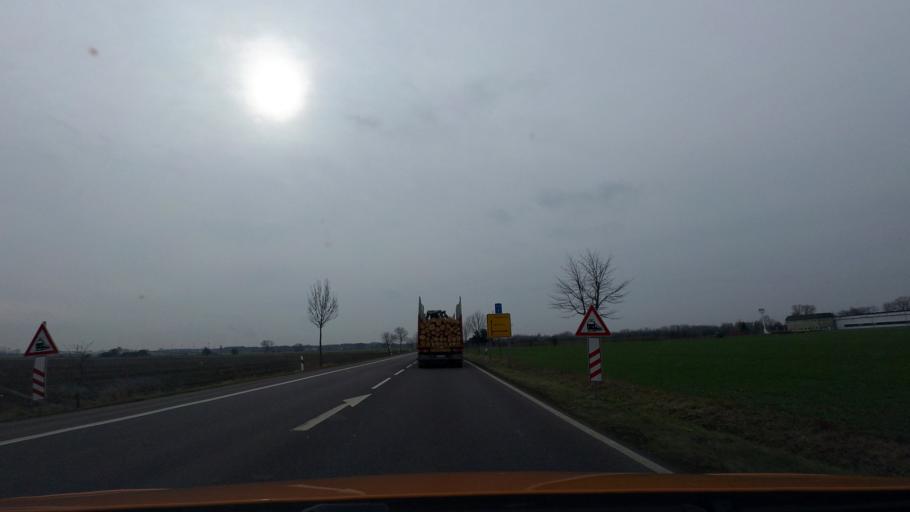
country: DE
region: Saxony-Anhalt
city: Gerwisch
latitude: 52.1563
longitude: 11.7392
